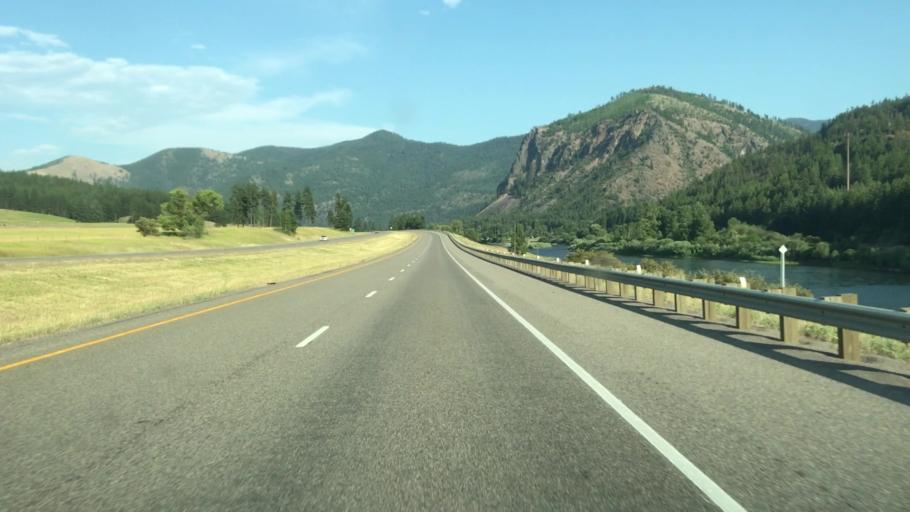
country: US
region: Montana
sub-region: Missoula County
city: Frenchtown
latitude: 46.9987
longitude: -114.4662
